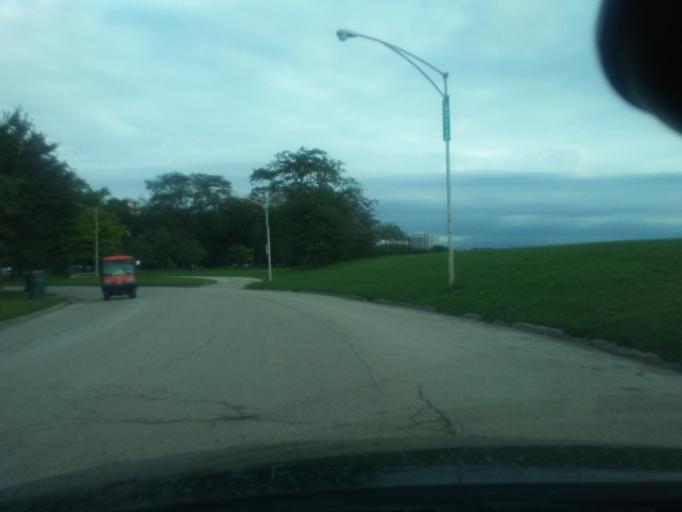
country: US
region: Illinois
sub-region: Cook County
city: Evanston
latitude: 41.9694
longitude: -87.6444
